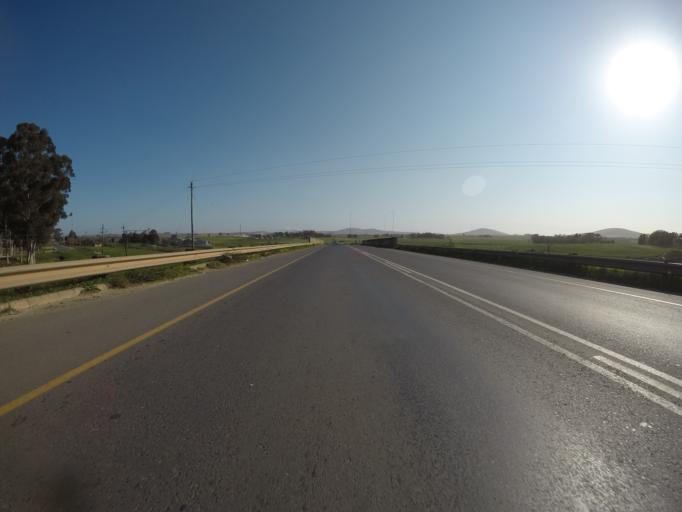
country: ZA
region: Western Cape
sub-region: City of Cape Town
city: Kraaifontein
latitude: -33.7823
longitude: 18.7128
